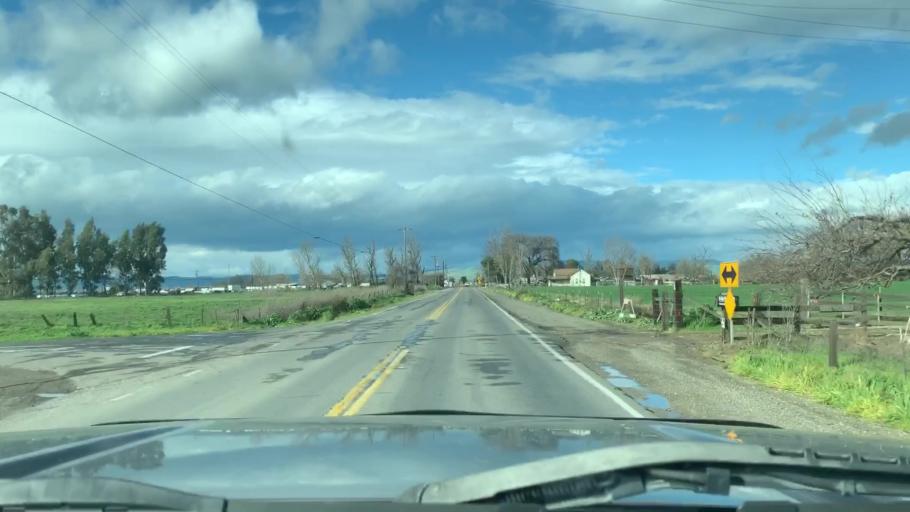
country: US
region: California
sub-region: Merced County
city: Los Banos
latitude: 37.1001
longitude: -120.9252
